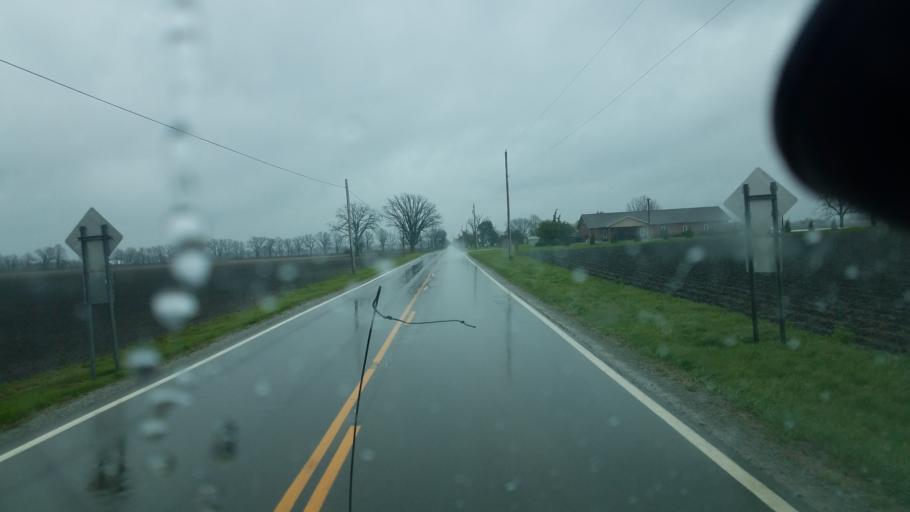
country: US
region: Ohio
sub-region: Wyandot County
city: Upper Sandusky
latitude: 40.8179
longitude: -83.3215
